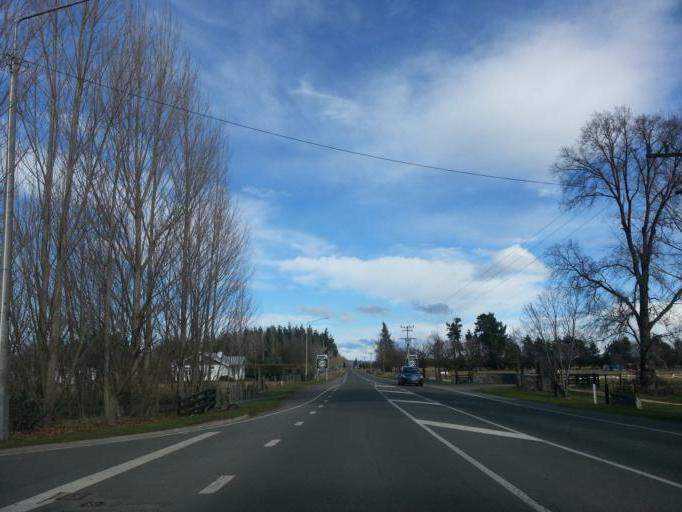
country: NZ
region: Canterbury
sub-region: Hurunui District
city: Amberley
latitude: -42.7759
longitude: 172.8466
